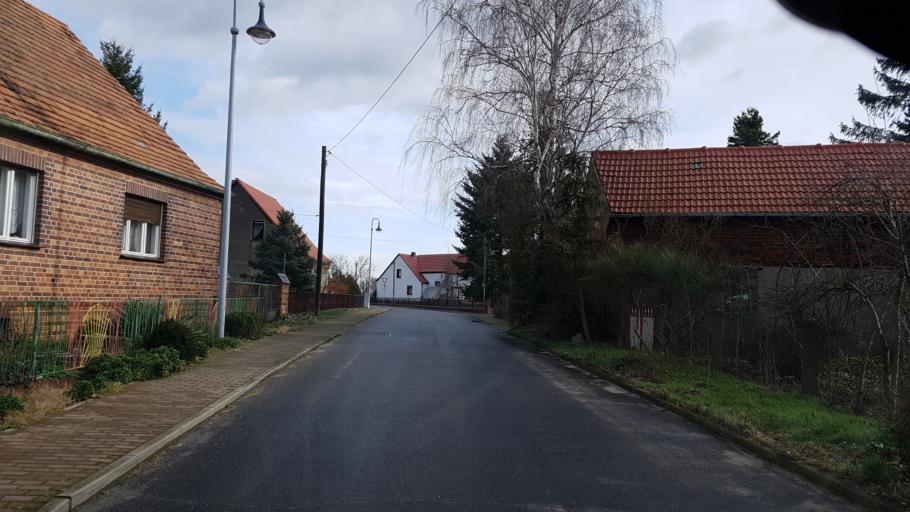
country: DE
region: Brandenburg
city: Schlieben
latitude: 51.7004
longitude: 13.4121
